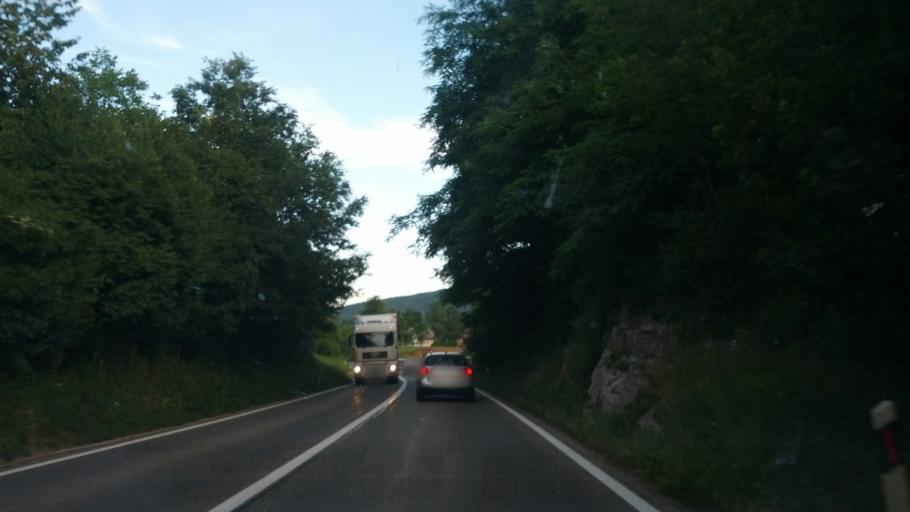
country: HR
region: Karlovacka
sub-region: Grad Karlovac
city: Slunj
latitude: 45.1304
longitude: 15.5643
